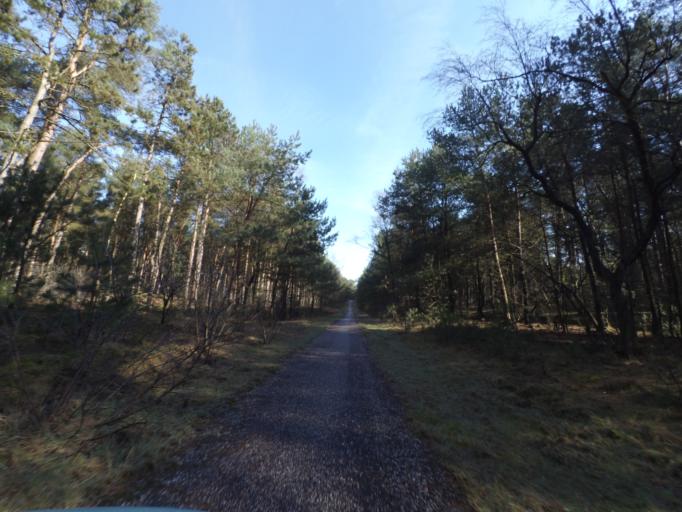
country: NL
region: Gelderland
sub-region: Gemeente Ede
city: Harskamp
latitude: 52.1710
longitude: 5.7356
